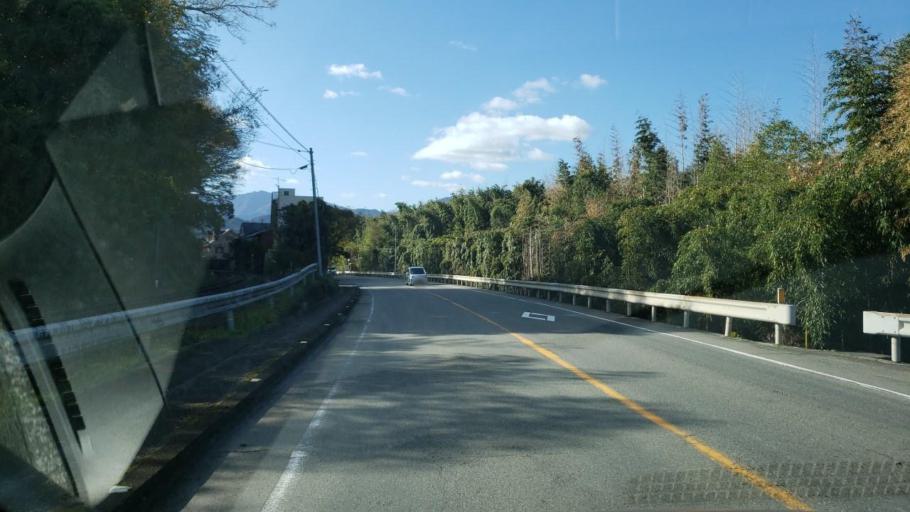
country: JP
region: Tokushima
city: Wakimachi
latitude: 34.0558
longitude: 134.1794
